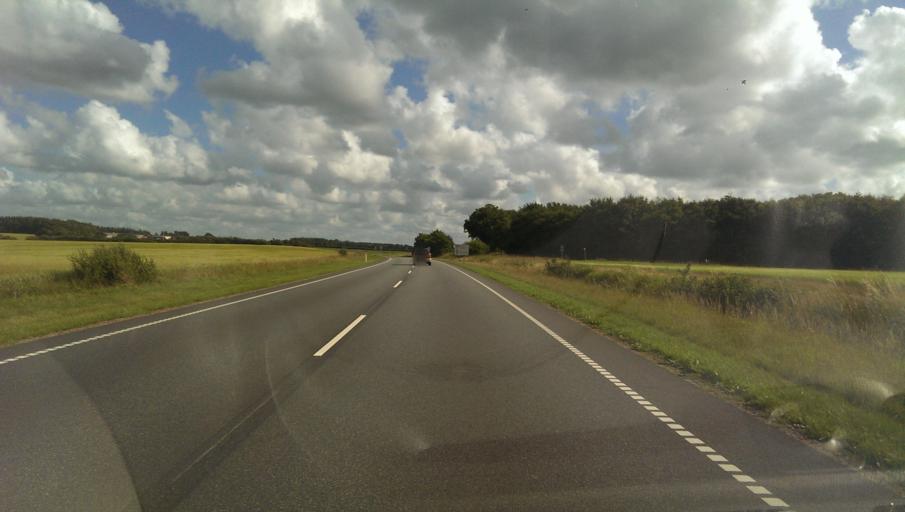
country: DK
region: South Denmark
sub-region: Varde Kommune
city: Varde
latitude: 55.6767
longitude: 8.4916
